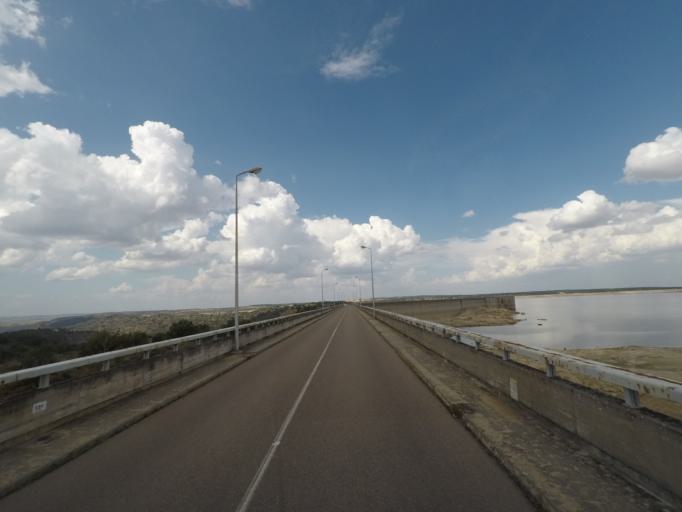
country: ES
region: Castille and Leon
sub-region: Provincia de Salamanca
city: Almendra
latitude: 41.2620
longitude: -6.3225
